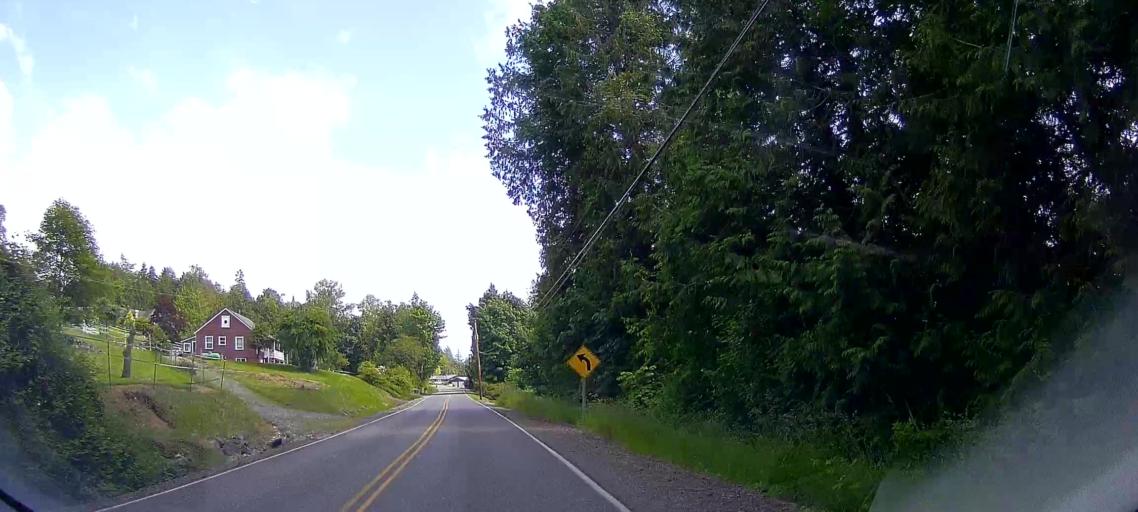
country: US
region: Washington
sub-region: Skagit County
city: Burlington
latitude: 48.5734
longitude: -122.3979
